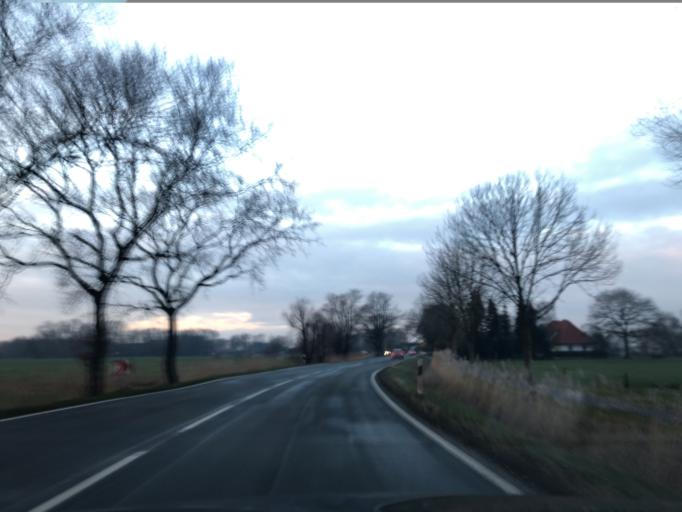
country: DE
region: Lower Saxony
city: Lemwerder
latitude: 53.1378
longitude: 8.5965
